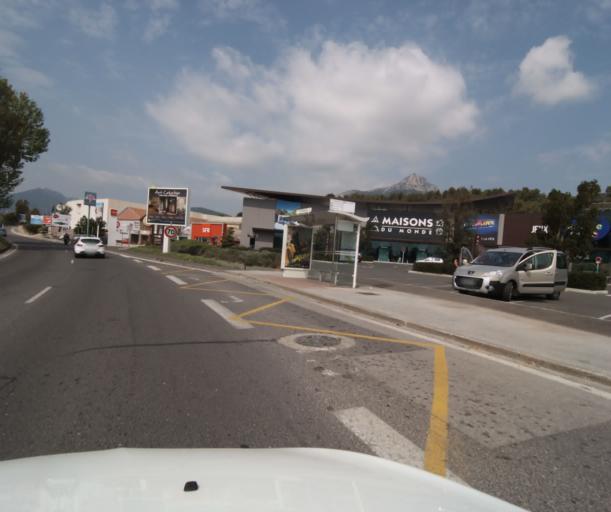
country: FR
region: Provence-Alpes-Cote d'Azur
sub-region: Departement du Var
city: La Garde
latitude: 43.1378
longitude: 6.0257
